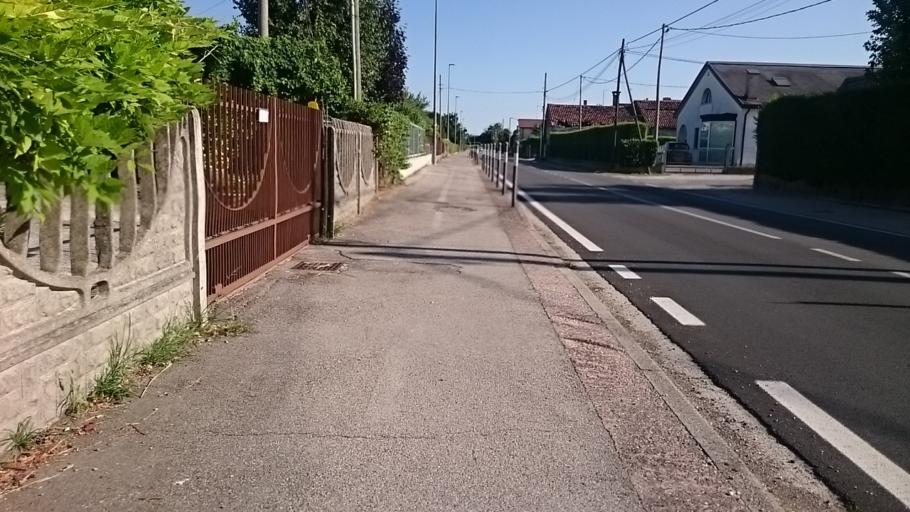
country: IT
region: Veneto
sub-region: Provincia di Padova
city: Villatora
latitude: 45.3688
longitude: 11.9639
